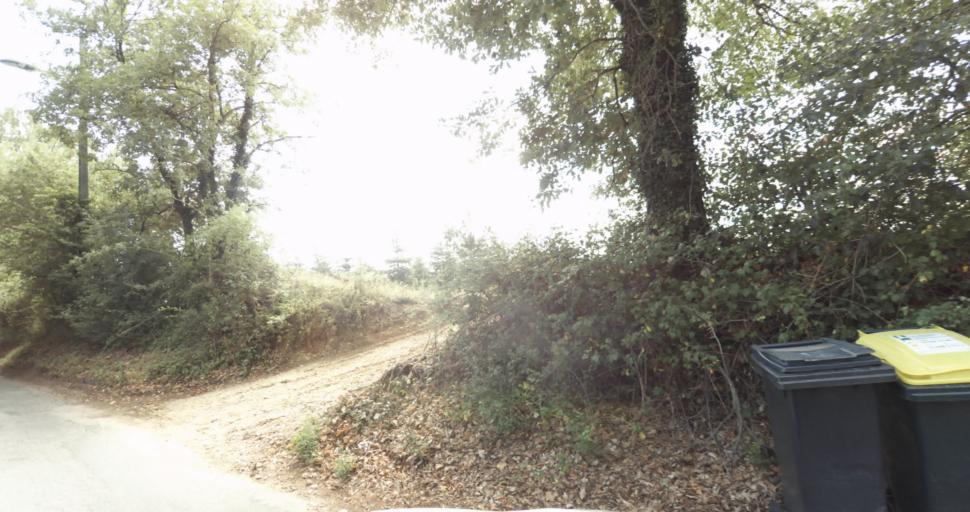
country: FR
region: Rhone-Alpes
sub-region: Departement du Rhone
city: Francheville
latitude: 45.7272
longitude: 4.7634
